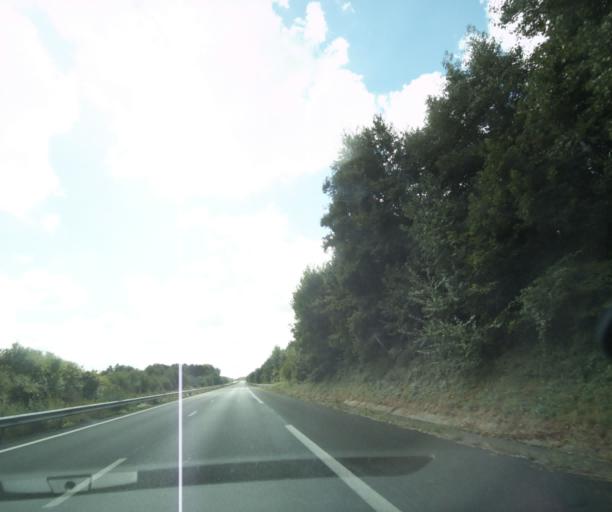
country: FR
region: Poitou-Charentes
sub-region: Departement de la Charente-Maritime
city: Cabariot
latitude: 45.9354
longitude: -0.8411
